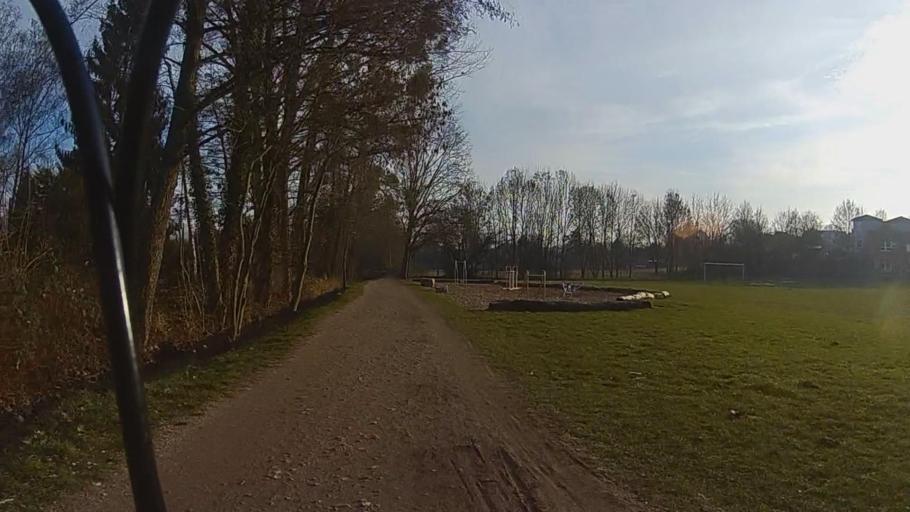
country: DE
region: Hesse
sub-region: Regierungsbezirk Darmstadt
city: Oberursel
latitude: 50.1976
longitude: 8.5801
